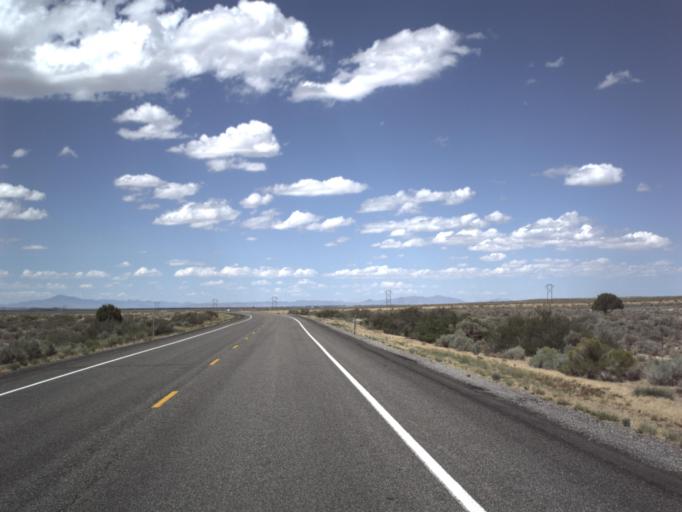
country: US
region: Utah
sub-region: Millard County
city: Fillmore
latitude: 39.1471
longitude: -112.3896
